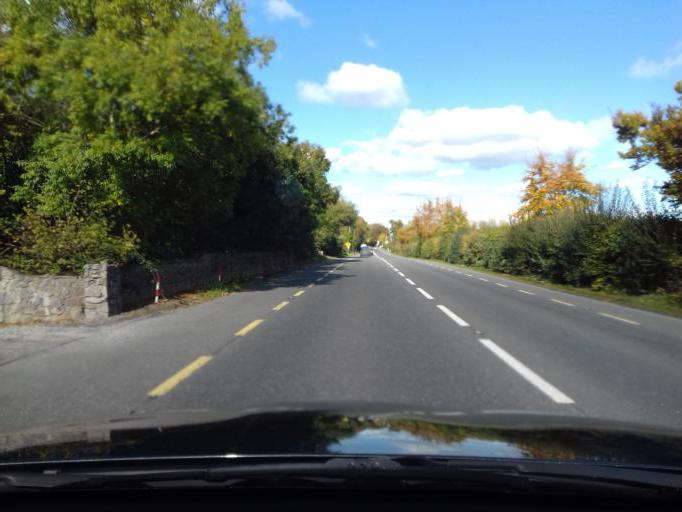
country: IE
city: Kentstown
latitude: 53.6345
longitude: -6.4942
